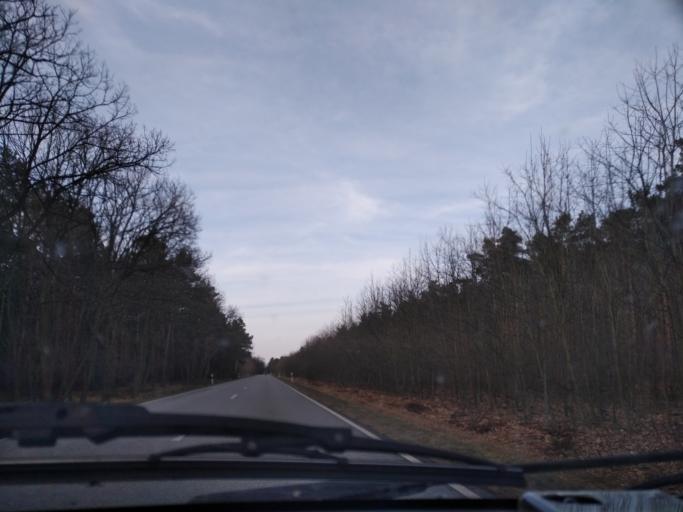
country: DE
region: Saxony-Anhalt
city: Holzdorf
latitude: 51.8770
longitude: 13.1438
